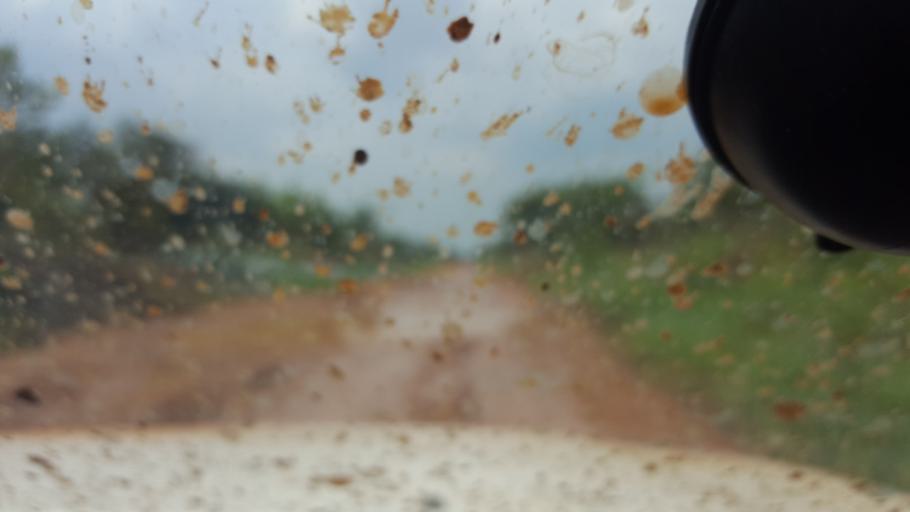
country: CD
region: Bandundu
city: Bandundu
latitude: -3.7613
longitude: 17.1515
